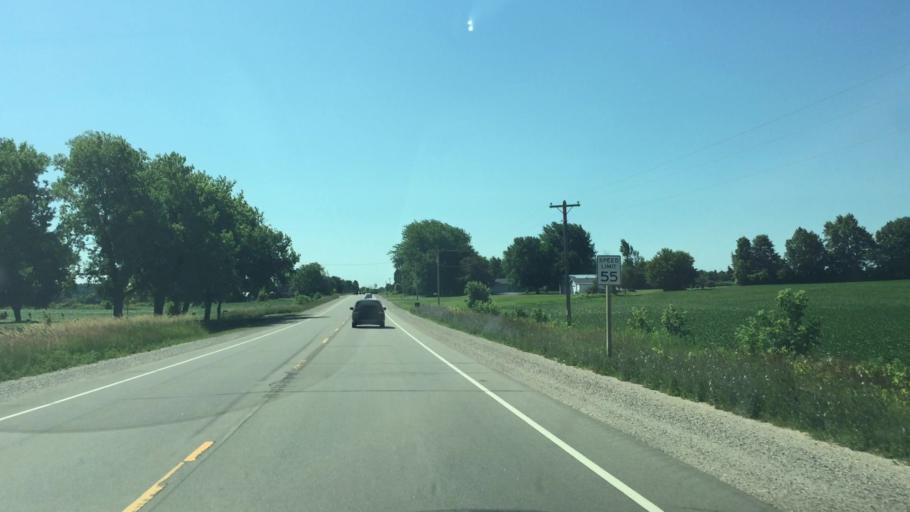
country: US
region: Wisconsin
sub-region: Calumet County
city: New Holstein
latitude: 43.9854
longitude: -88.1184
